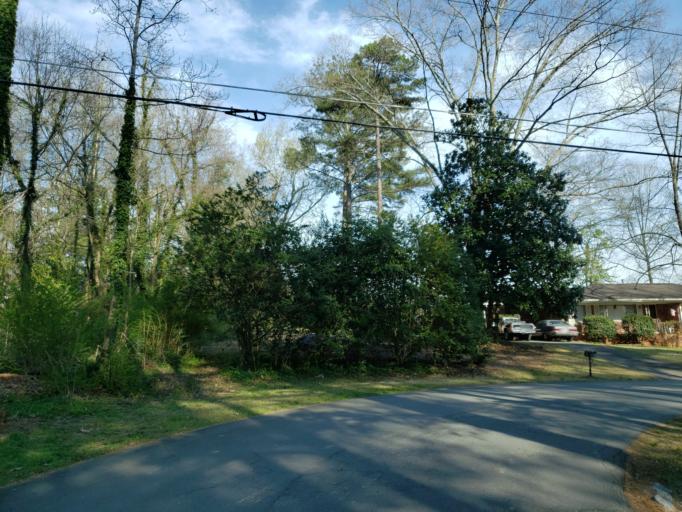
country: US
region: Georgia
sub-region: Cobb County
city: Marietta
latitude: 33.9800
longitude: -84.4668
